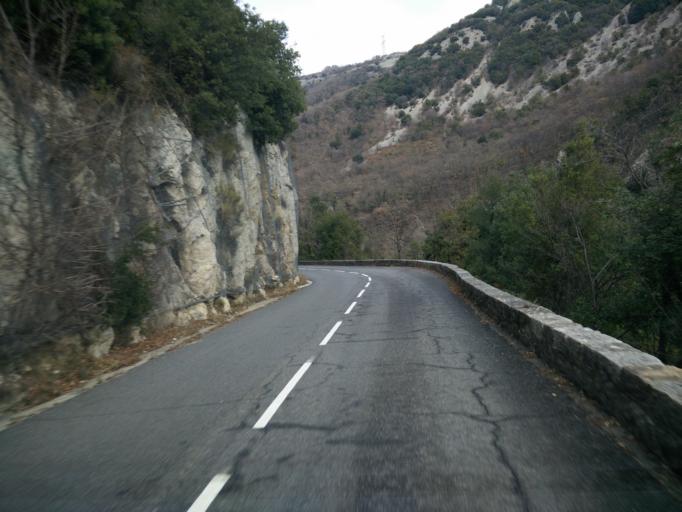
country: FR
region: Provence-Alpes-Cote d'Azur
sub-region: Departement des Alpes-Maritimes
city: Tourrettes-sur-Loup
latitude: 43.7580
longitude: 6.9897
